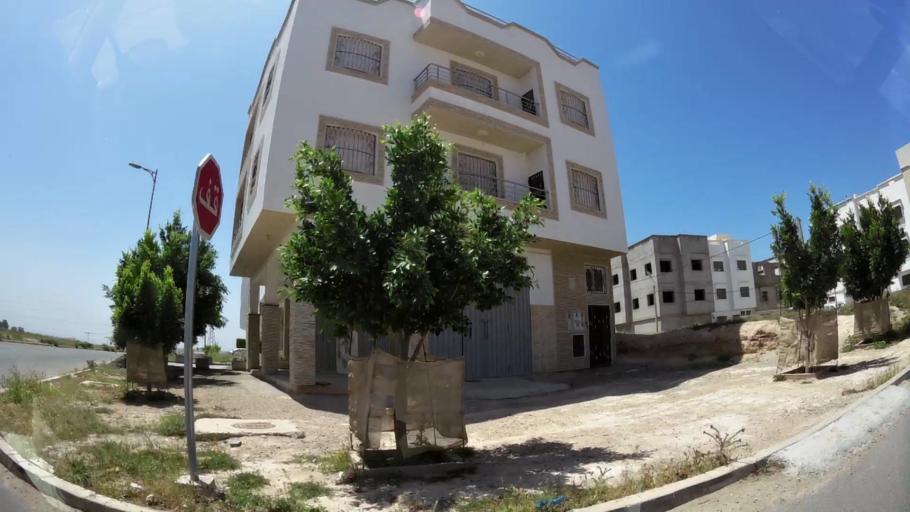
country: MA
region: Oued ed Dahab-Lagouira
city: Dakhla
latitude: 30.4267
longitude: -9.5524
